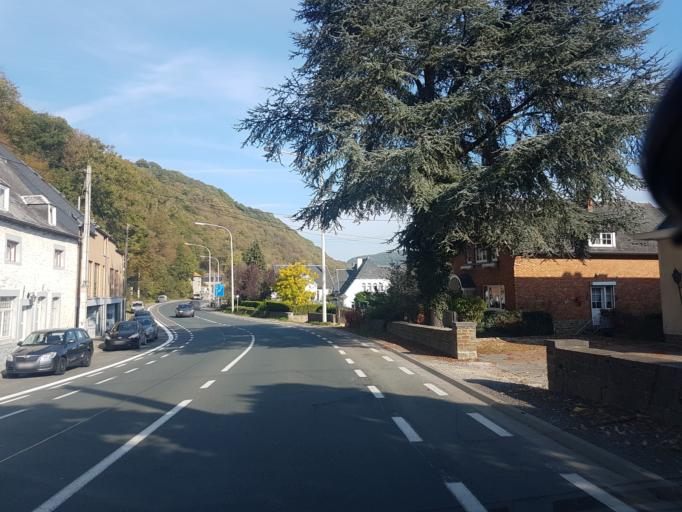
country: BE
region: Wallonia
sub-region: Province de Namur
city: Profondeville
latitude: 50.3621
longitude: 4.8705
